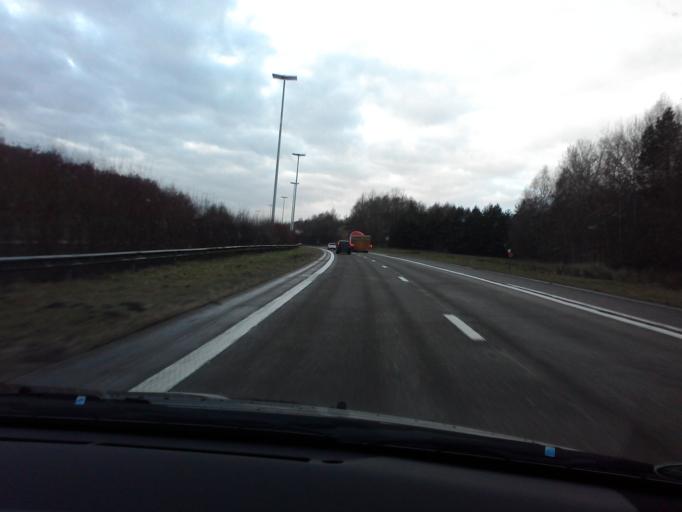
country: BE
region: Wallonia
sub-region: Province de Liege
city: Sprimont
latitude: 50.5471
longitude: 5.6608
